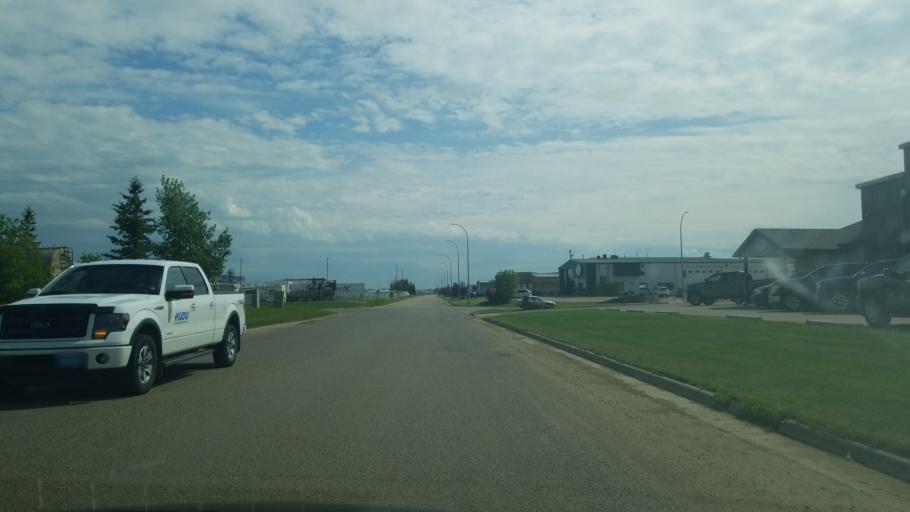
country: CA
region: Saskatchewan
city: Lloydminster
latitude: 53.2922
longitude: -110.0368
